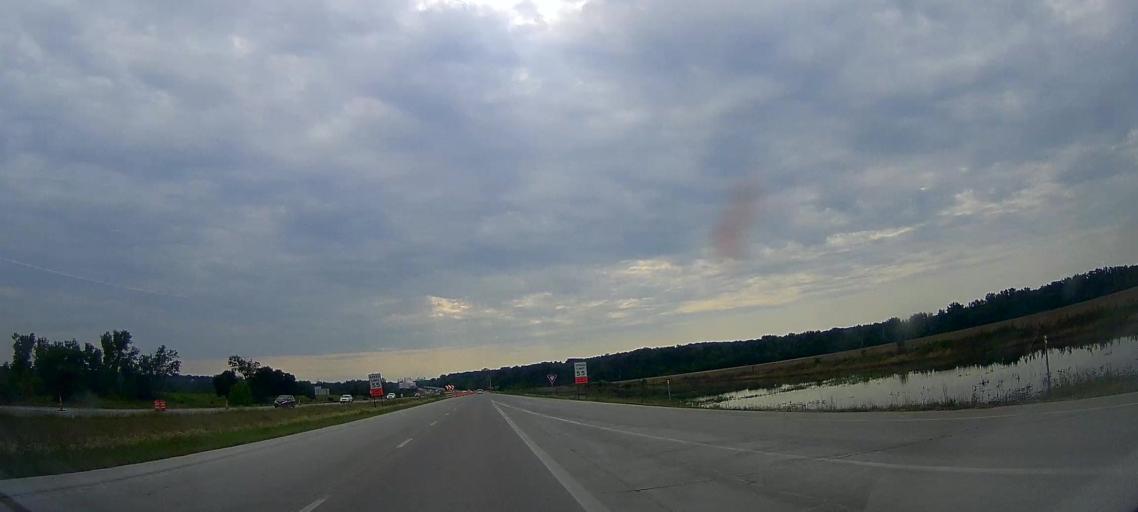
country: US
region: Iowa
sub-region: Pottawattamie County
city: Carter Lake
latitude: 41.3467
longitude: -95.9413
